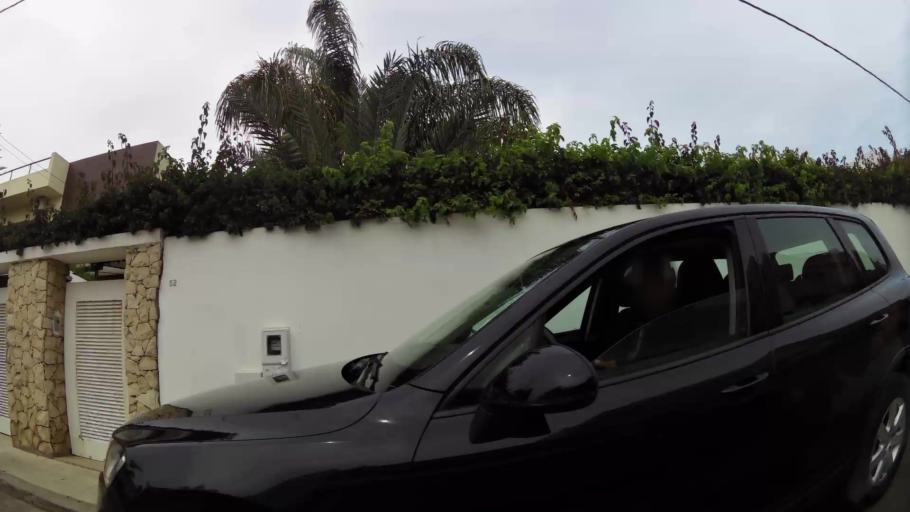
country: MA
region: Rabat-Sale-Zemmour-Zaer
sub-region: Rabat
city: Rabat
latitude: 34.0297
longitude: -6.8125
